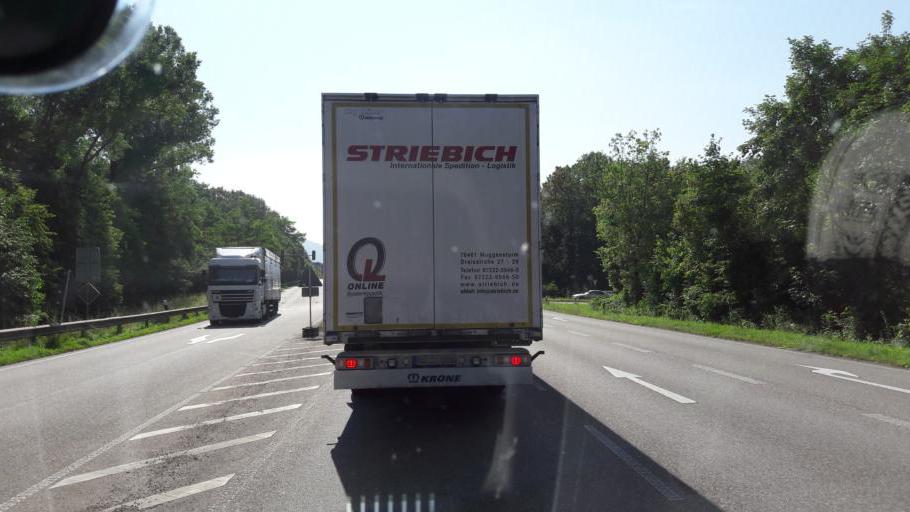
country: DE
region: Baden-Wuerttemberg
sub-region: Karlsruhe Region
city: Otigheim
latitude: 48.8639
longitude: 8.2409
